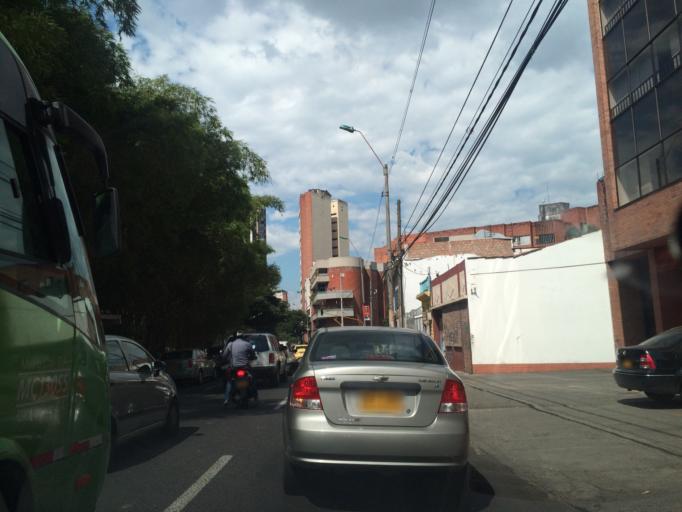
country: CO
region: Valle del Cauca
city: Cali
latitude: 3.4508
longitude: -76.5435
